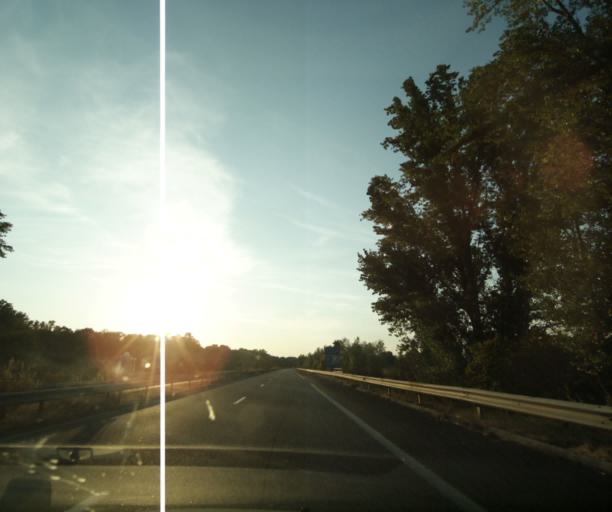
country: FR
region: Aquitaine
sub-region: Departement du Lot-et-Garonne
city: Layrac
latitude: 44.1238
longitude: 0.7061
